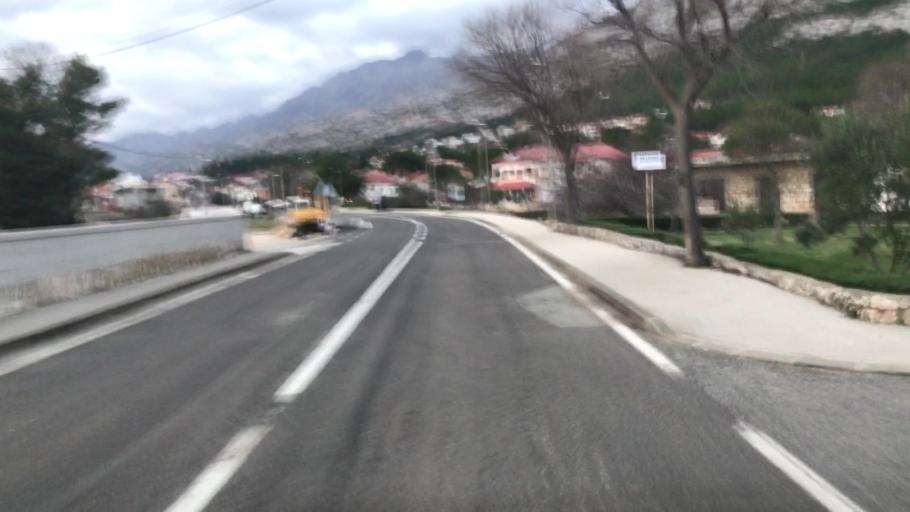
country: HR
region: Zadarska
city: Starigrad
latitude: 44.2925
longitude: 15.4417
